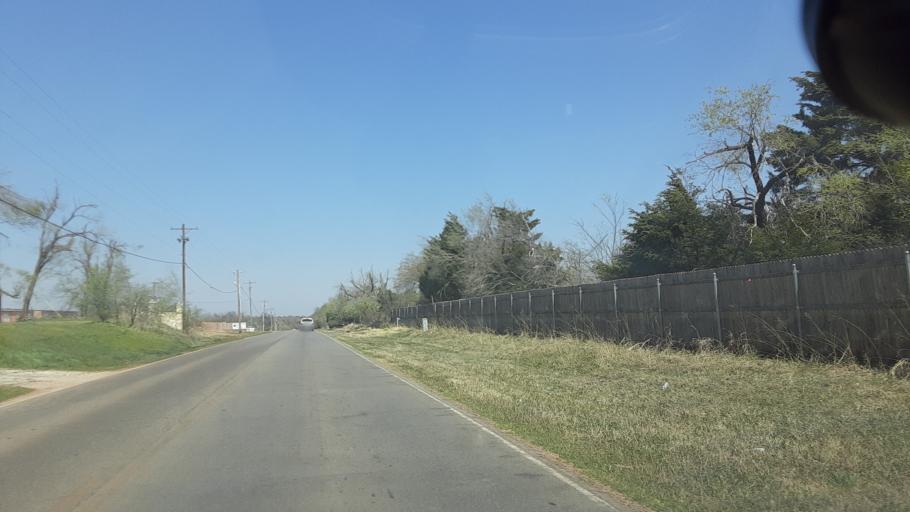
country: US
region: Oklahoma
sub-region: Oklahoma County
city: Edmond
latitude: 35.7319
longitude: -97.4783
